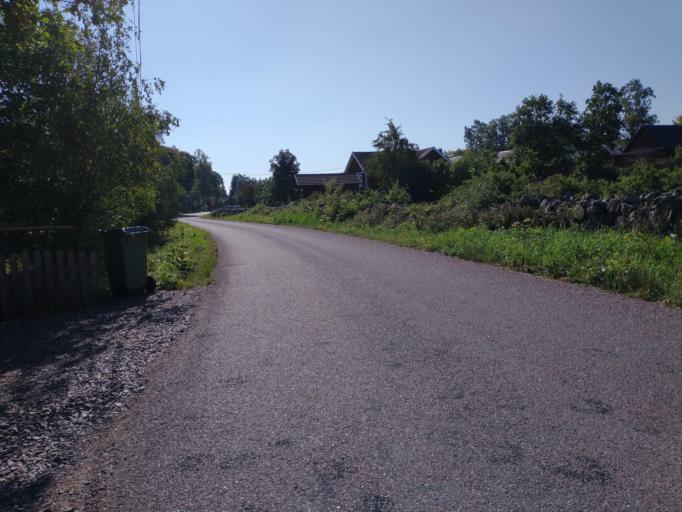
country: SE
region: Kalmar
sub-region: Kalmar Kommun
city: Lindsdal
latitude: 56.7871
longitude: 16.2923
